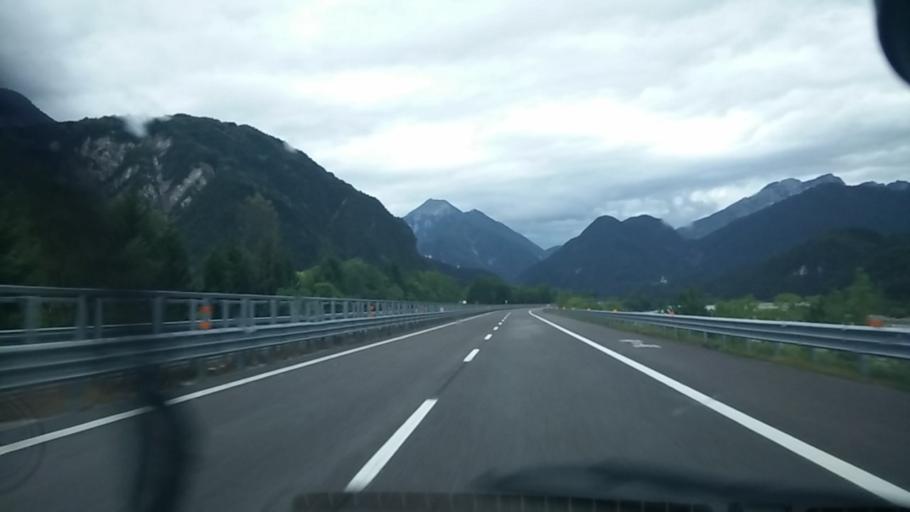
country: IT
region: Friuli Venezia Giulia
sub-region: Provincia di Udine
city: Resiutta
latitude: 46.3942
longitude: 13.2269
